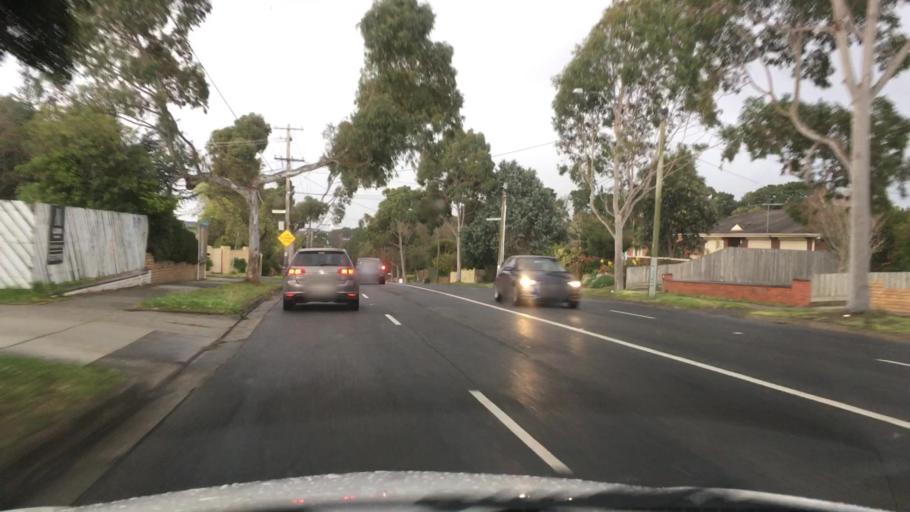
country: AU
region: Victoria
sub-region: Monash
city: Ashwood
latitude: -37.8755
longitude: 145.1103
